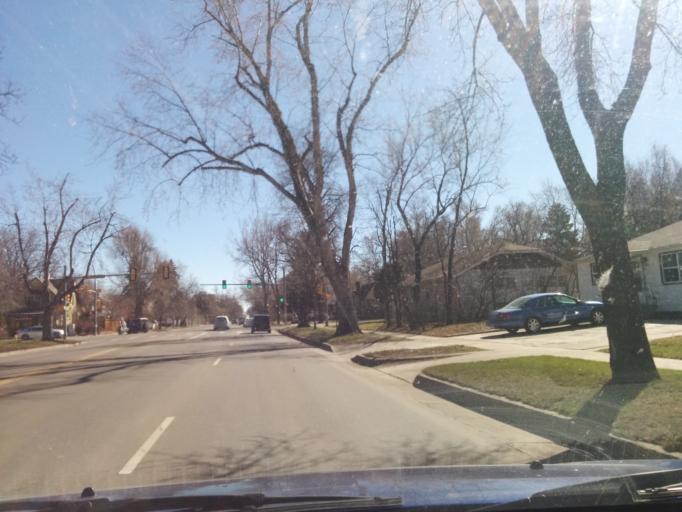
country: US
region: Colorado
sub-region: Larimer County
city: Fort Collins
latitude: 40.5816
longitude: -105.0889
